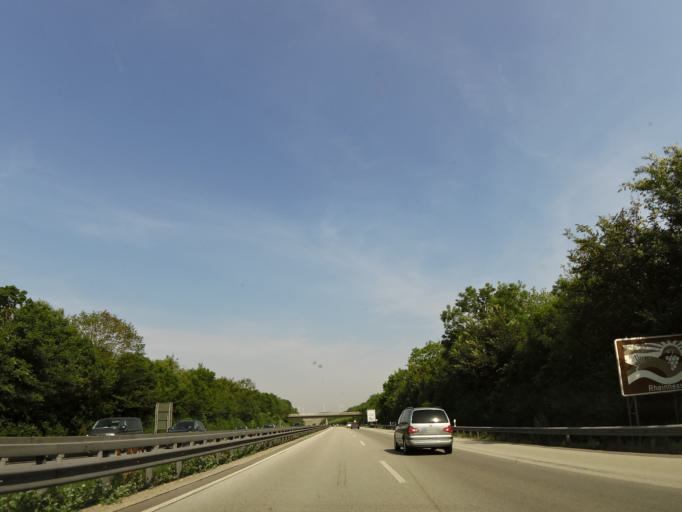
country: DE
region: Rheinland-Pfalz
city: Gundheim
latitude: 49.6899
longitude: 8.2381
